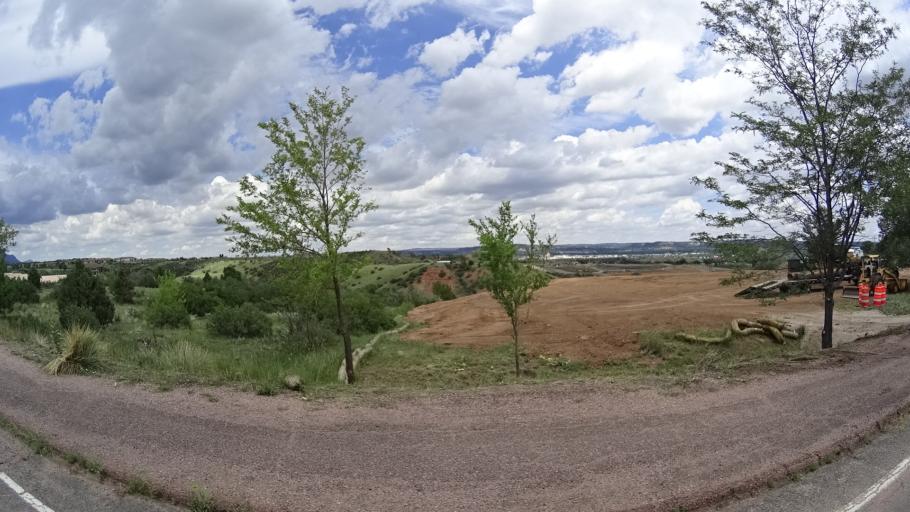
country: US
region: Colorado
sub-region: El Paso County
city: Colorado Springs
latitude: 38.8629
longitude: -104.8512
